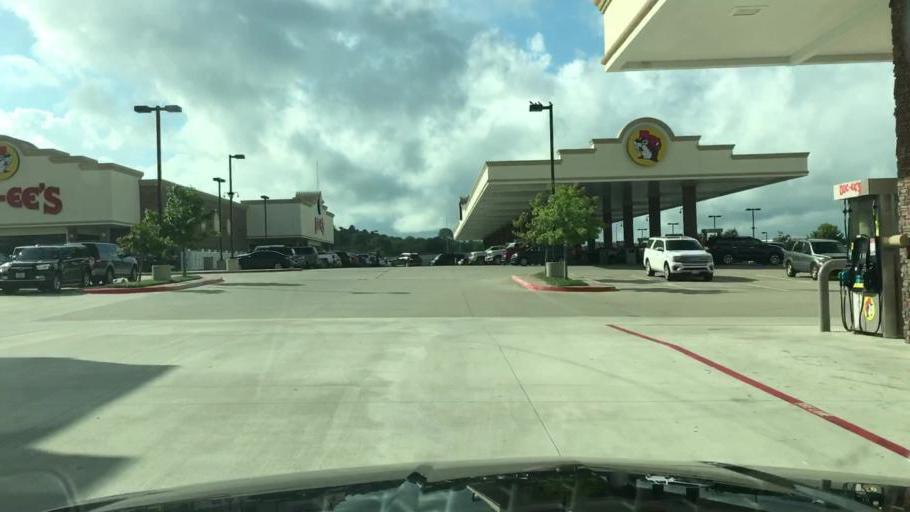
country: US
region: Texas
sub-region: Bastrop County
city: Bastrop
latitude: 30.1081
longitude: -97.3064
